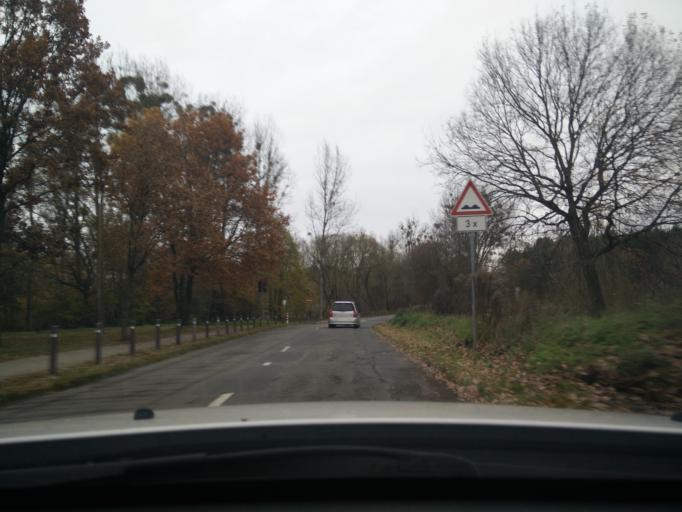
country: DE
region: Berlin
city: Staaken
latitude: 52.5644
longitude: 13.1322
